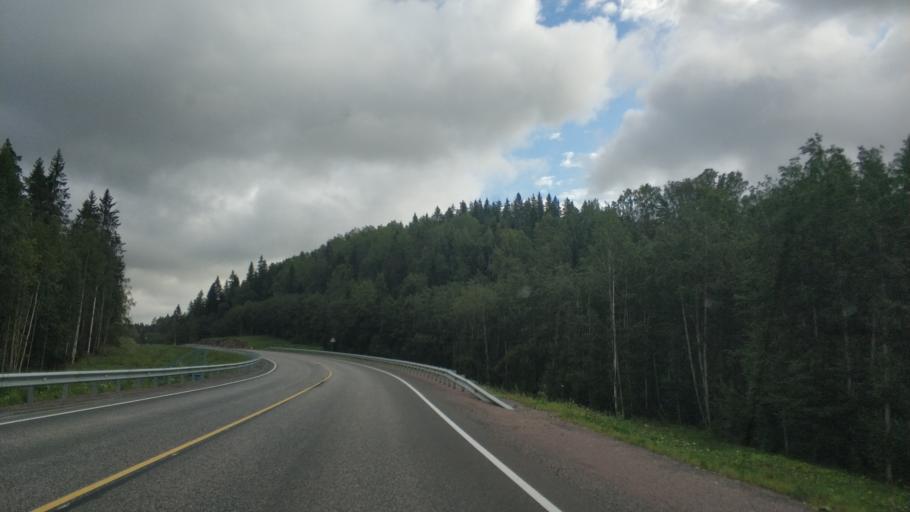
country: RU
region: Republic of Karelia
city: Khelyulya
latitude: 61.8319
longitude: 30.6378
